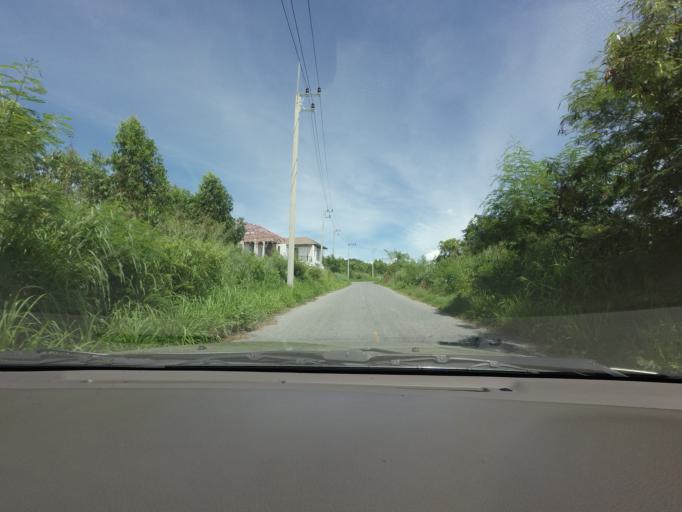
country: TH
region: Chon Buri
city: Si Racha
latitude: 13.2433
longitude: 100.9573
